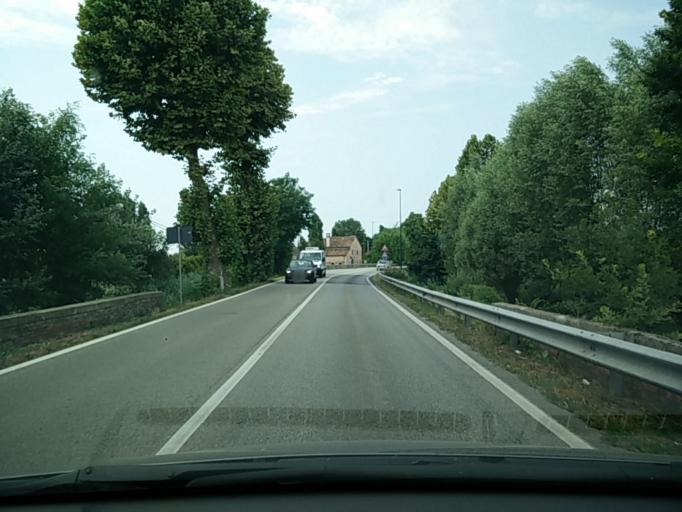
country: IT
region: Veneto
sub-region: Provincia di Treviso
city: San Floriano-Olmi
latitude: 45.6681
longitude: 12.3178
